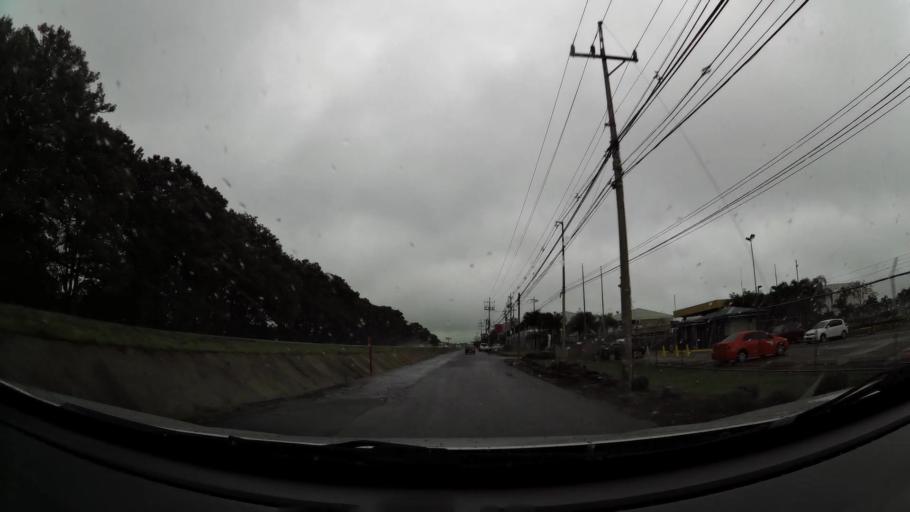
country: CR
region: Alajuela
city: Carrillos
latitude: 9.9950
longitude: -84.2583
